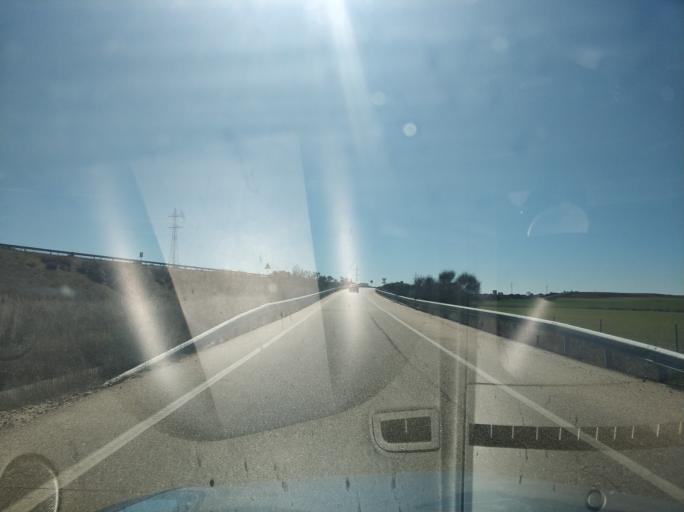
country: ES
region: Castille and Leon
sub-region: Provincia de Salamanca
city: Castellanos de Moriscos
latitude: 41.0139
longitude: -5.5877
